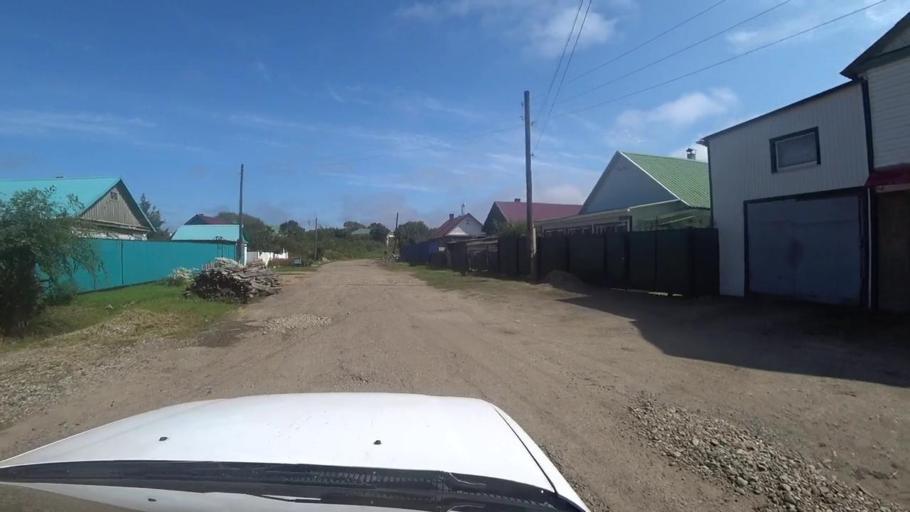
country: RU
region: Primorskiy
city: Dal'nerechensk
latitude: 45.9280
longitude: 133.7245
